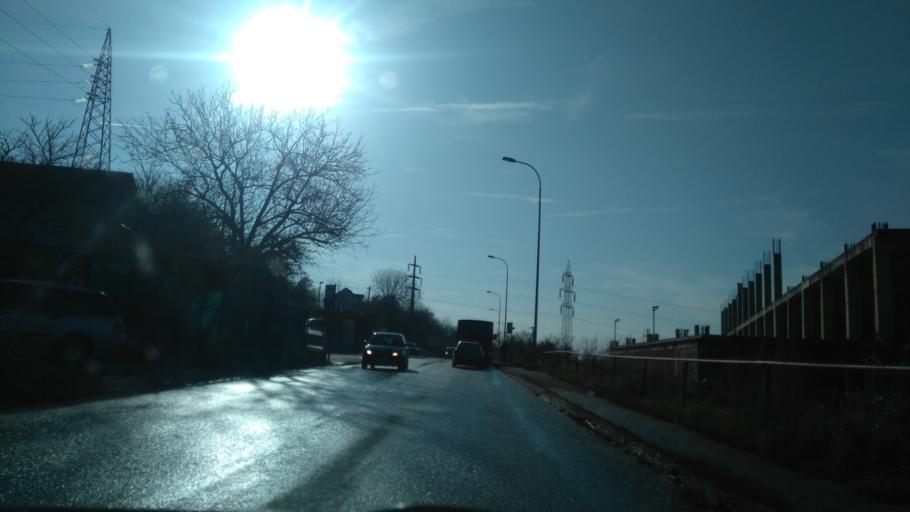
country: RS
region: Central Serbia
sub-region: Belgrade
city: Cukarica
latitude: 44.7498
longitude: 20.4007
